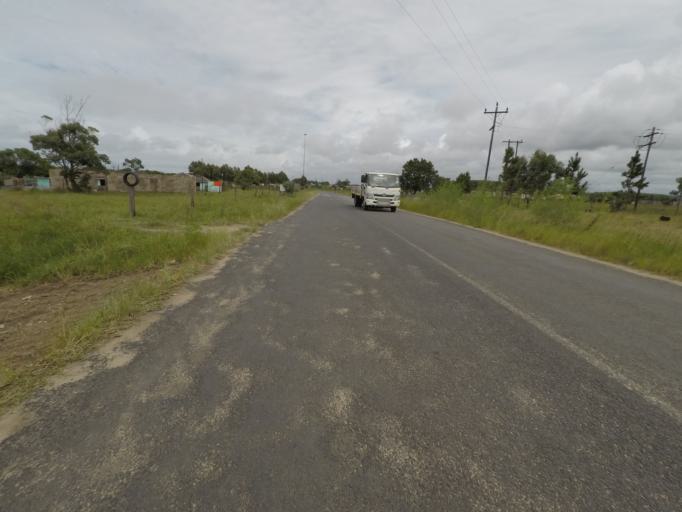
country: ZA
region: KwaZulu-Natal
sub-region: uThungulu District Municipality
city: eSikhawini
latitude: -28.9106
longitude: 31.8669
